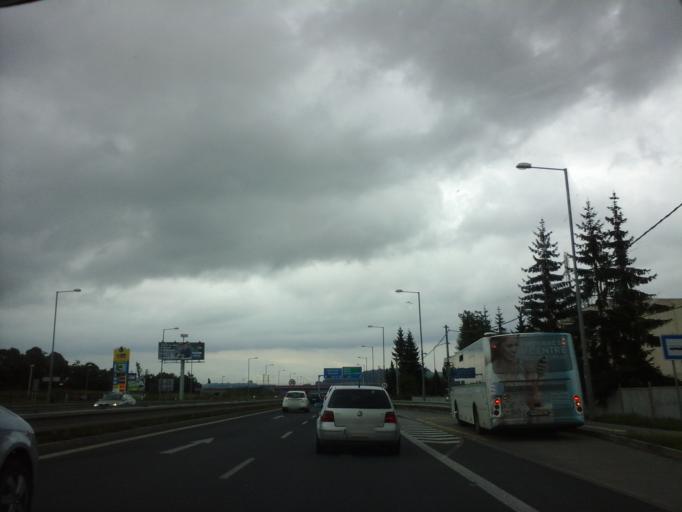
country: SK
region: Presovsky
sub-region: Okres Poprad
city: Poprad
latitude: 49.0674
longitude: 20.3231
